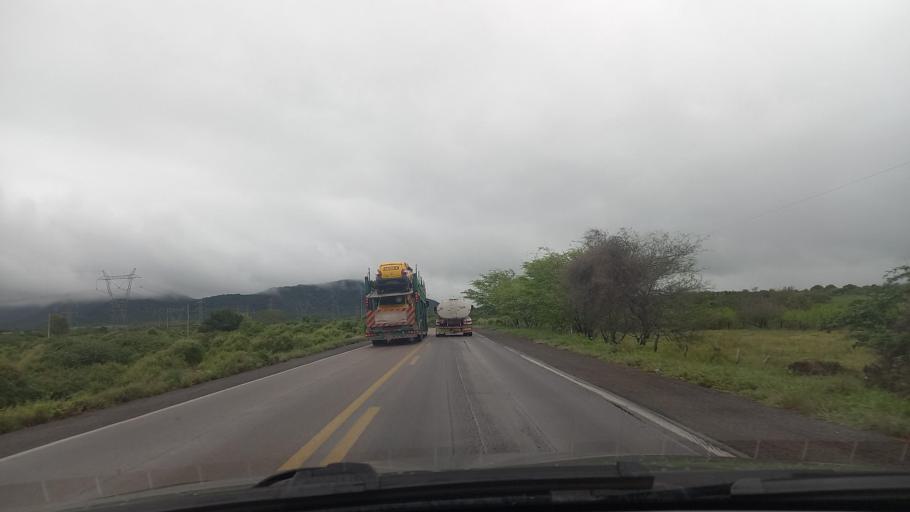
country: BR
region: Alagoas
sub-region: Agua Branca
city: Agua Branca
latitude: -9.3240
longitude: -37.9661
